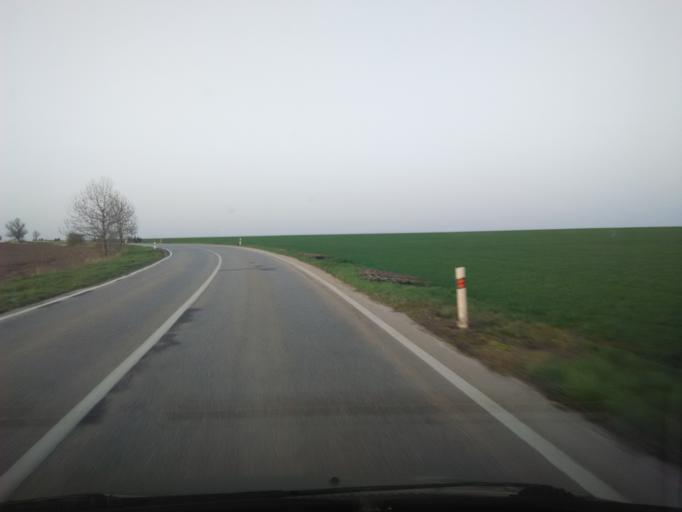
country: SK
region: Nitriansky
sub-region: Okres Nitra
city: Nitra
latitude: 48.2353
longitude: 18.0064
